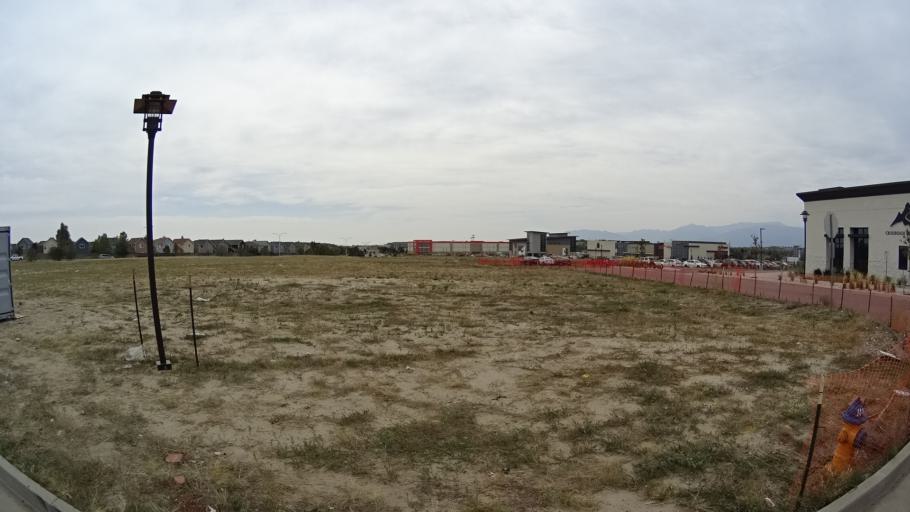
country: US
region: Colorado
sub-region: El Paso County
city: Cimarron Hills
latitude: 38.9249
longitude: -104.7169
